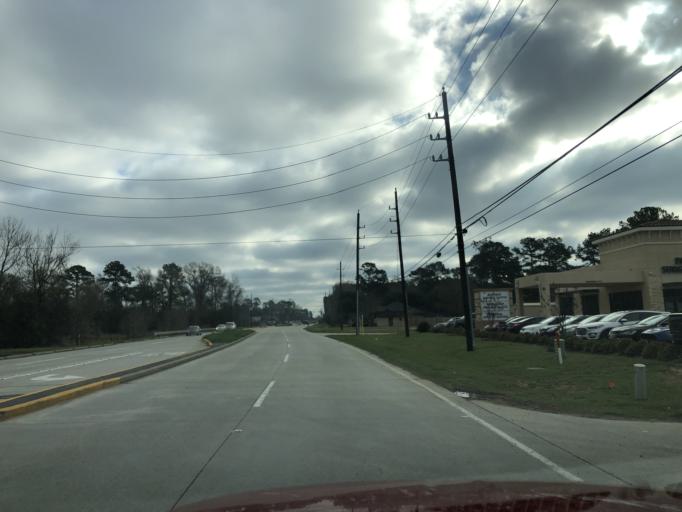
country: US
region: Texas
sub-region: Harris County
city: Spring
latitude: 30.0826
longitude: -95.4678
